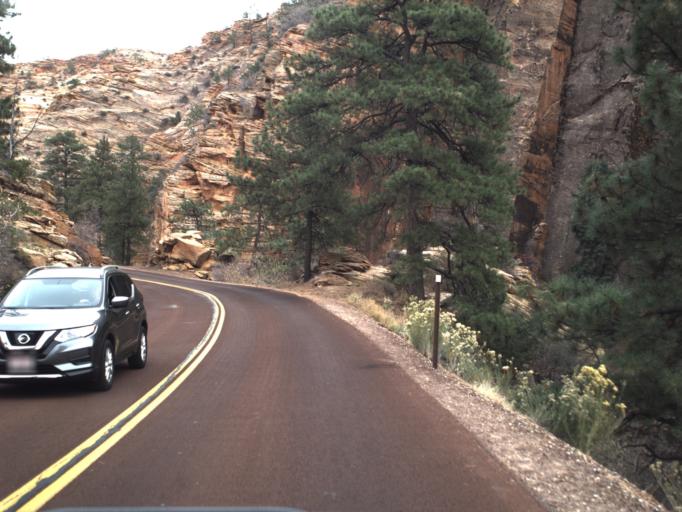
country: US
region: Utah
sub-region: Washington County
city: Hildale
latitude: 37.2135
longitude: -112.9329
